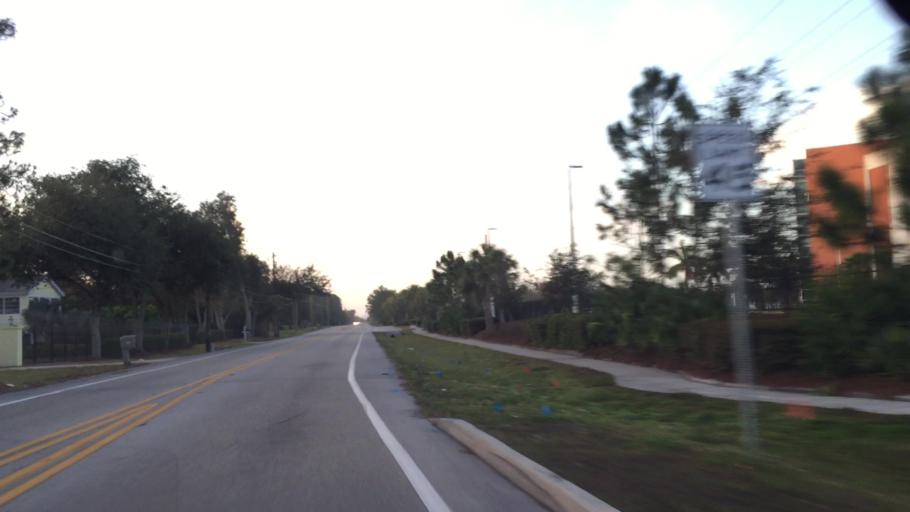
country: US
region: Florida
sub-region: Lee County
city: Pine Manor
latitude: 26.5815
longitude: -81.8473
